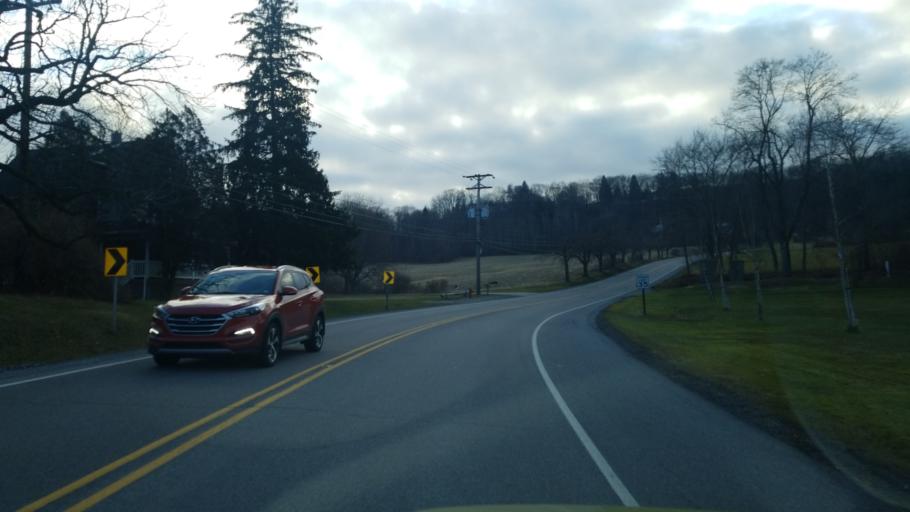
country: US
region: Pennsylvania
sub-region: Clearfield County
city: Clearfield
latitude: 41.0066
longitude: -78.4280
